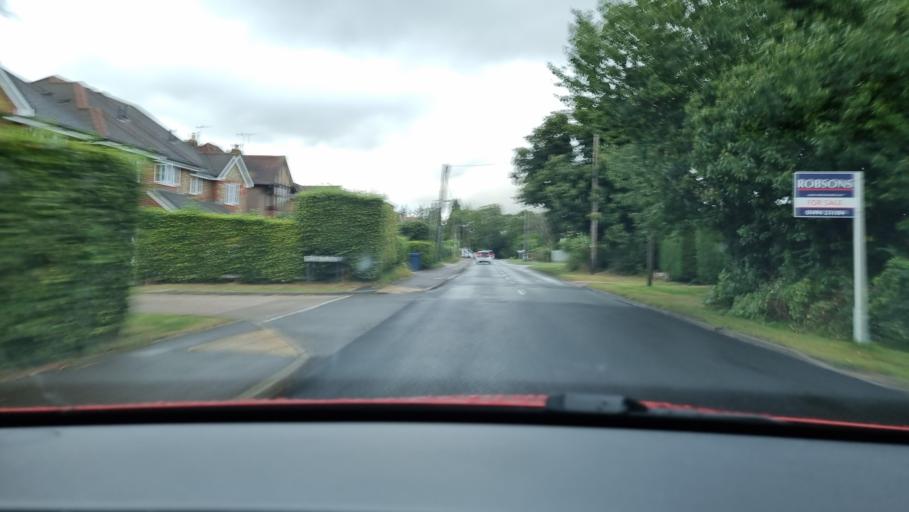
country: GB
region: England
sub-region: Buckinghamshire
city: Chesham
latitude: 51.7118
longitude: -0.5966
